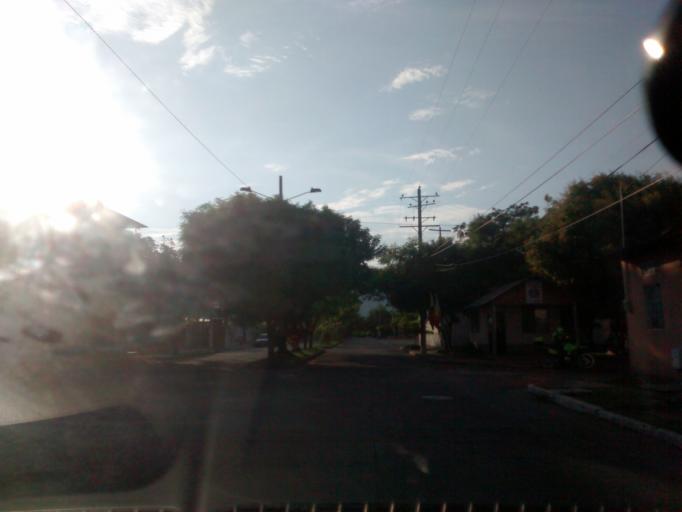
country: CO
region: Tolima
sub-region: Flandes
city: Flandes
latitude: 4.2928
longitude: -74.8204
